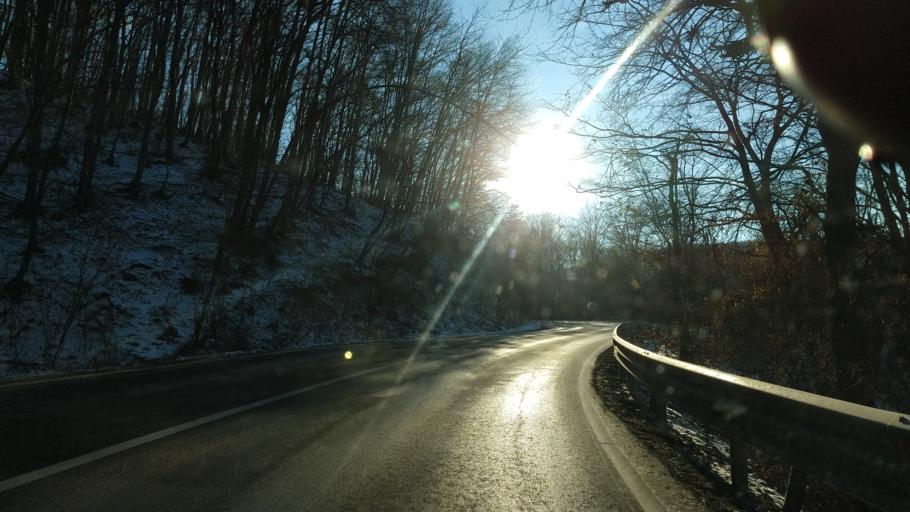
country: RO
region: Bacau
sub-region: Comuna Luizi-Calugara
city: Luizi-Calugara
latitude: 46.5494
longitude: 26.8188
